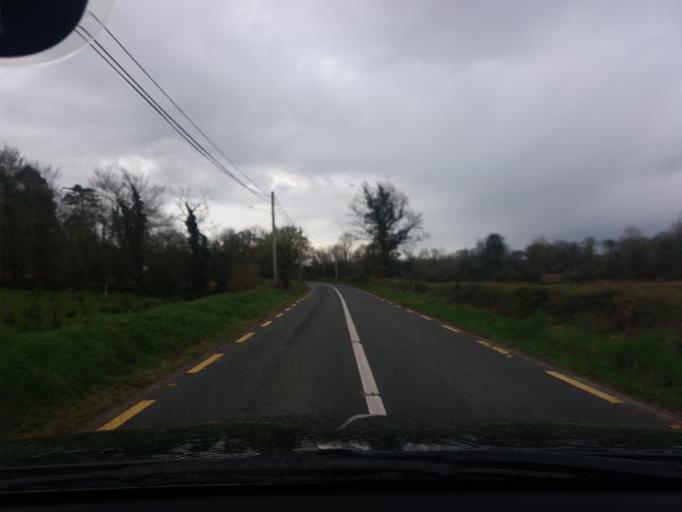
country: IE
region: Ulster
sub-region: An Cabhan
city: Ballyconnell
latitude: 54.1471
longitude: -7.7072
